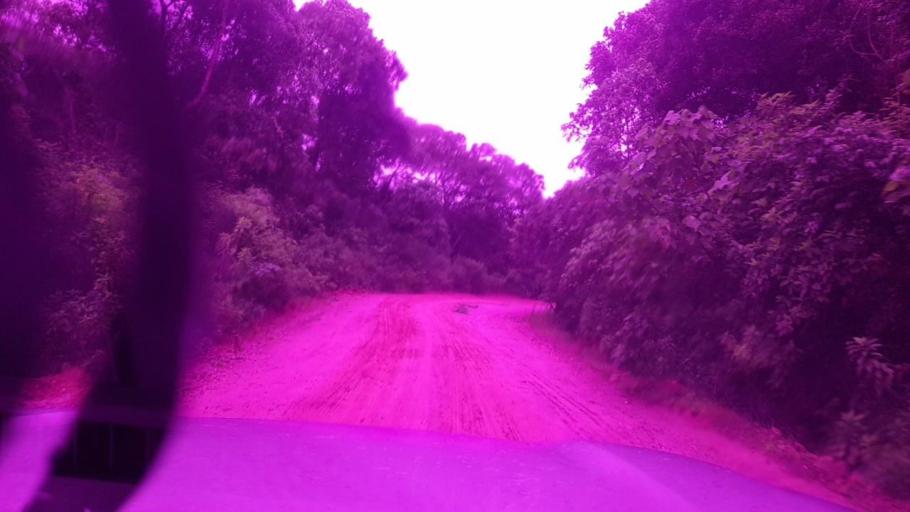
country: ET
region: Southern Nations, Nationalities, and People's Region
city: Bonga
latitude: 7.5051
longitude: 36.1050
